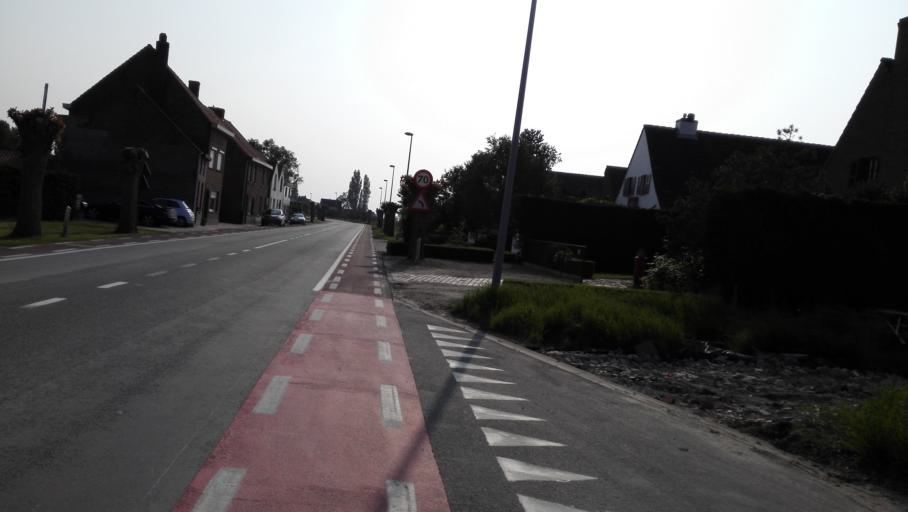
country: BE
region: Flanders
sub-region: Provincie West-Vlaanderen
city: Zuienkerke
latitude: 51.2901
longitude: 3.1827
